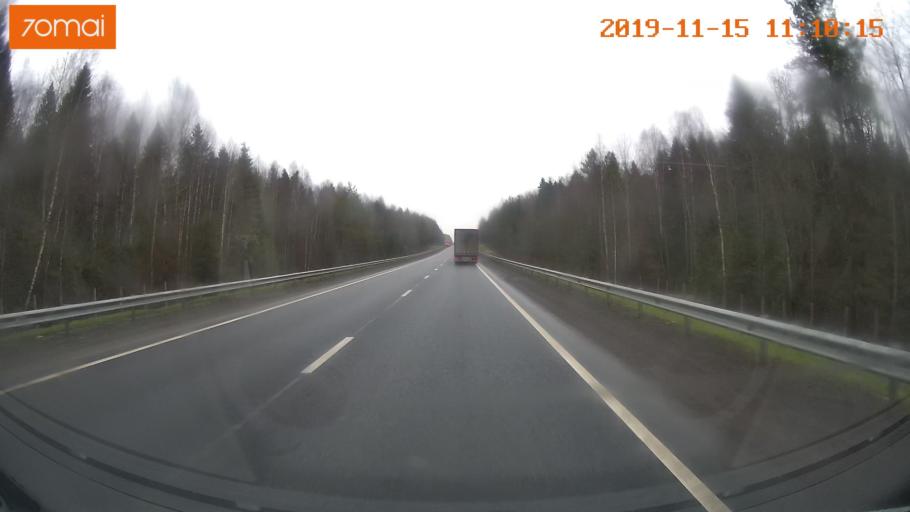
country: RU
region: Vologda
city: Chebsara
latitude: 59.1212
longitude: 39.1173
